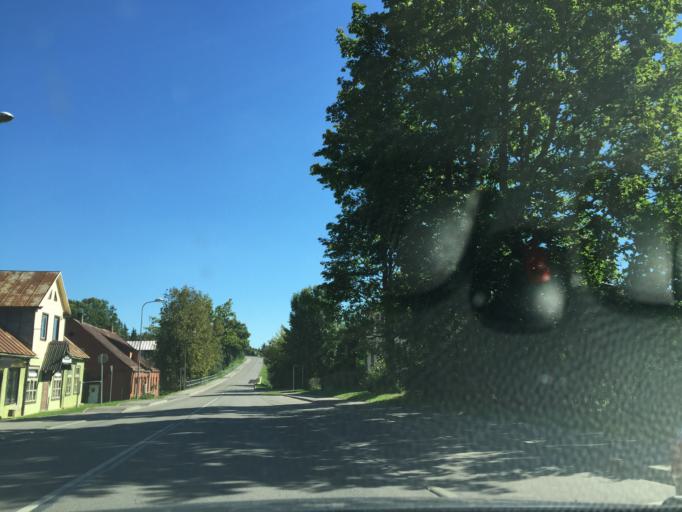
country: LV
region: Akniste
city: Akniste
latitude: 56.1594
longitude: 25.7524
